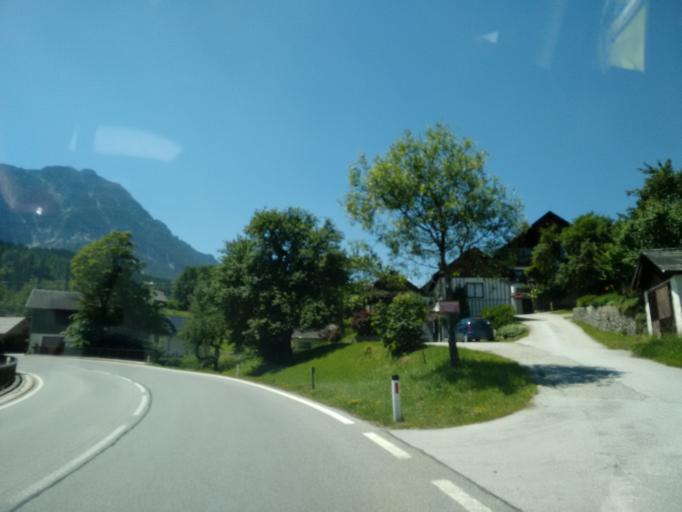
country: AT
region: Styria
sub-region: Politischer Bezirk Liezen
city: Altaussee
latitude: 47.6296
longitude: 13.7219
